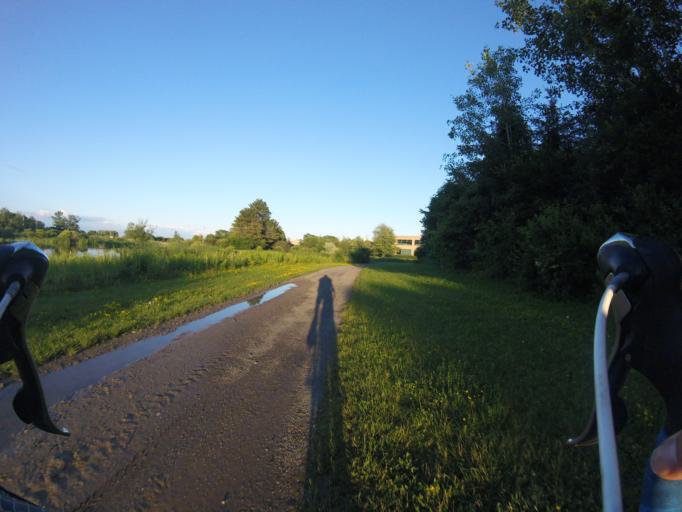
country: CA
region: Ontario
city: Bells Corners
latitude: 45.3536
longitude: -75.8547
